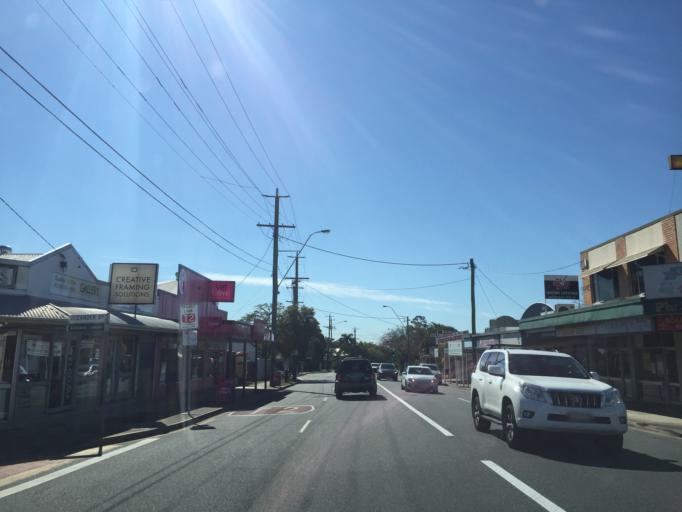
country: AU
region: Queensland
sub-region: Brisbane
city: Milton
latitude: -27.4461
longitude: 152.9866
